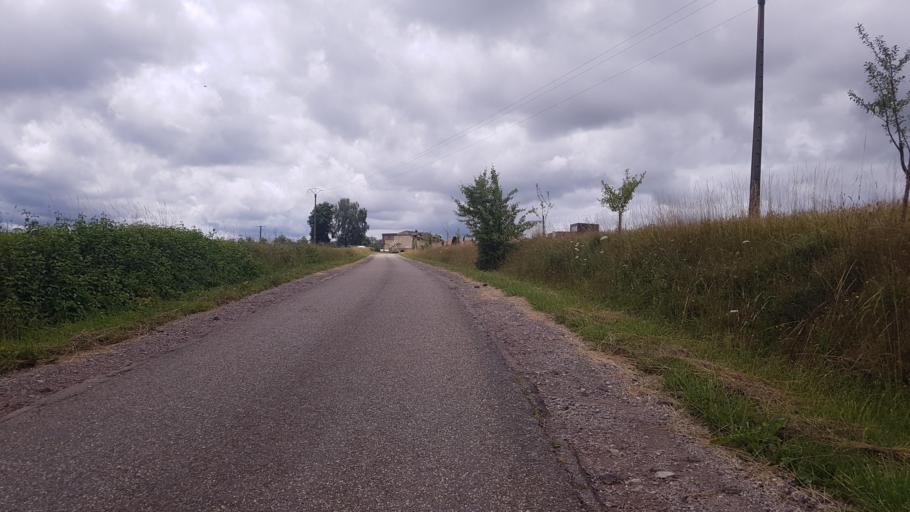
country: FR
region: Lorraine
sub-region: Departement de la Moselle
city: Niderviller
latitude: 48.7055
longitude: 7.0831
